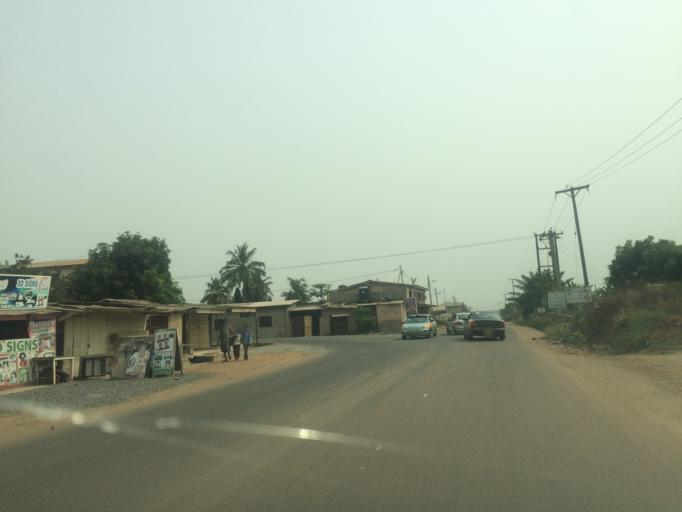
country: GH
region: Greater Accra
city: Nungua
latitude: 5.6078
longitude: -0.0865
